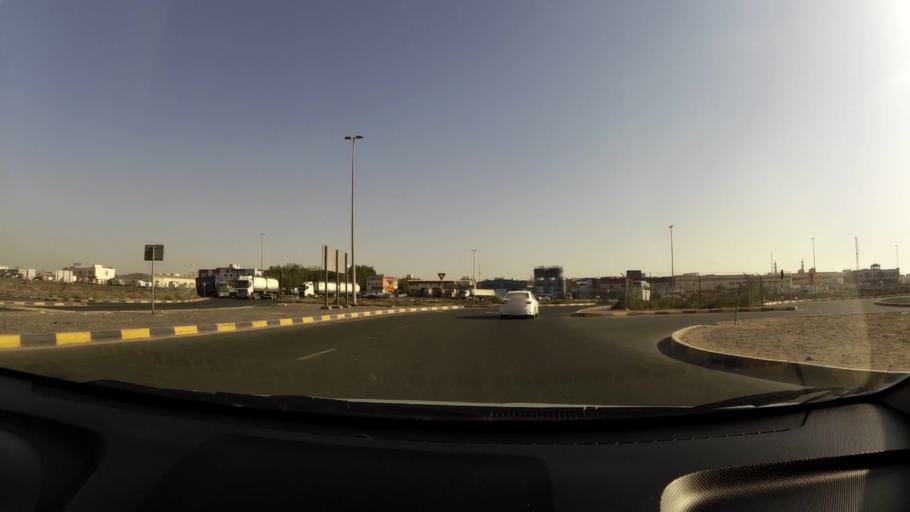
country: AE
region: Ajman
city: Ajman
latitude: 25.4428
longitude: 55.5493
